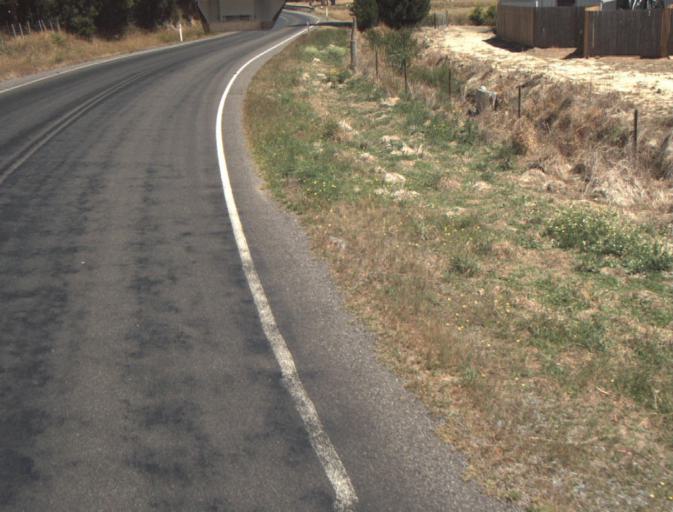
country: AU
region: Tasmania
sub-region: Launceston
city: Newstead
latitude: -41.3277
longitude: 147.3560
